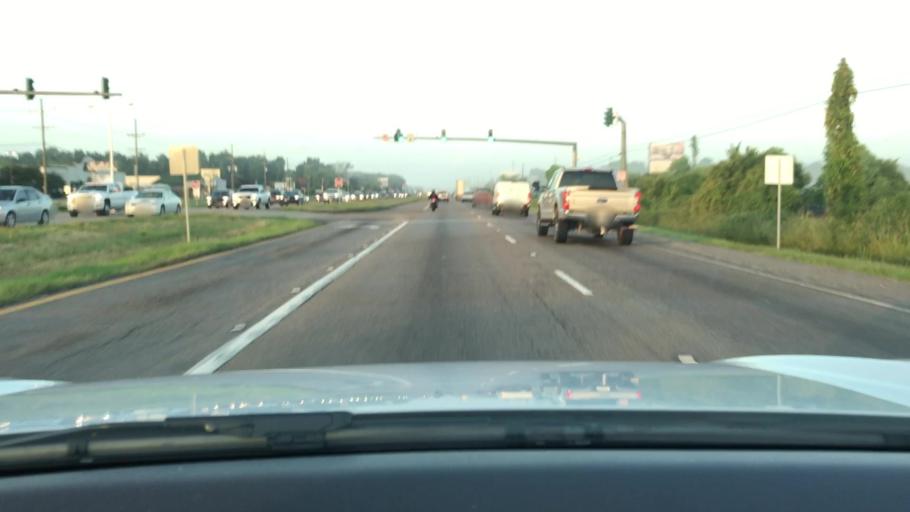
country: US
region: Louisiana
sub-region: West Baton Rouge Parish
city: Port Allen
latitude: 30.4218
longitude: -91.2192
